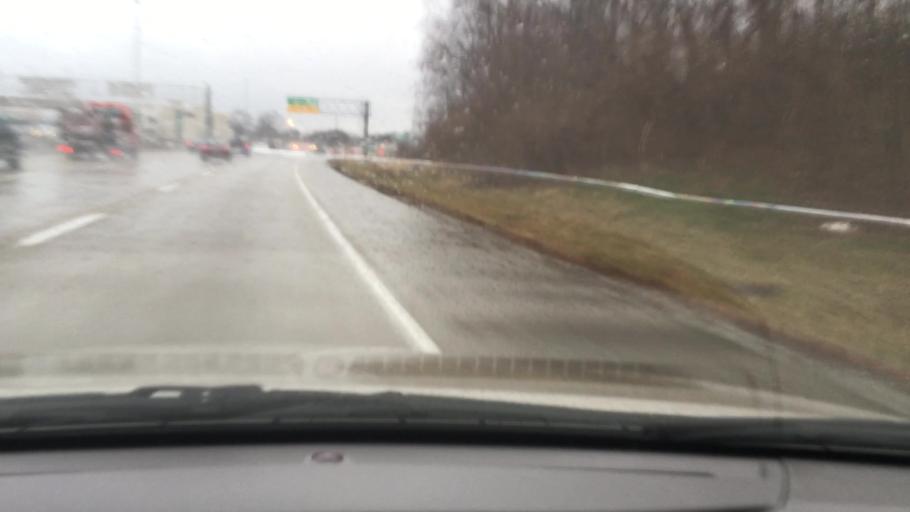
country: US
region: Indiana
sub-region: Marion County
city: Meridian Hills
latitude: 39.9185
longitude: -86.1124
